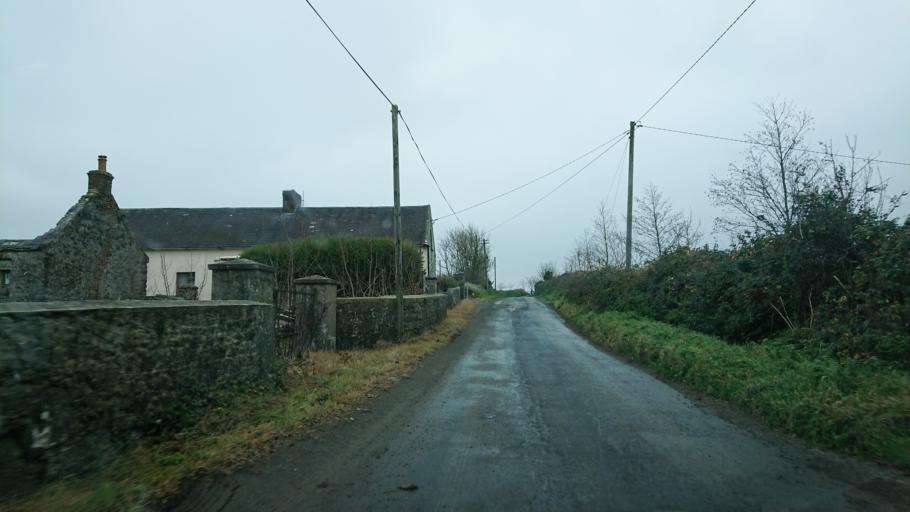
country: IE
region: Munster
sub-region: Waterford
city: Dunmore East
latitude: 52.1694
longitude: -7.0205
